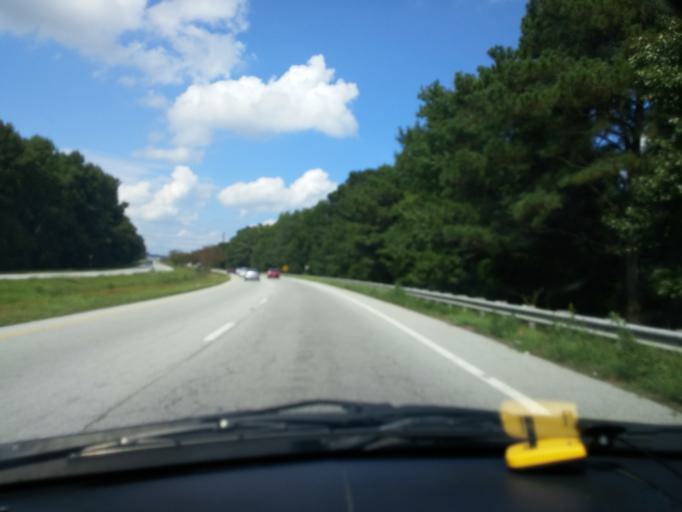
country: US
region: North Carolina
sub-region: Pitt County
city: Greenville
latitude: 35.6105
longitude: -77.3283
